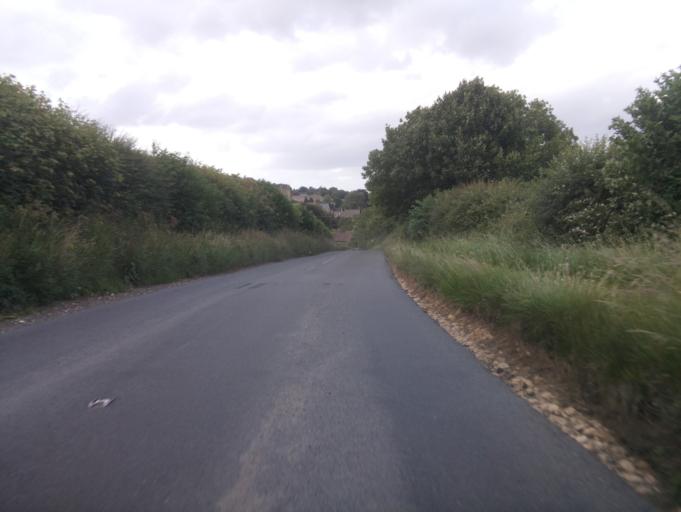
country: GB
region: England
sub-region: Gloucestershire
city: Chipping Campden
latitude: 52.0087
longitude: -1.7618
